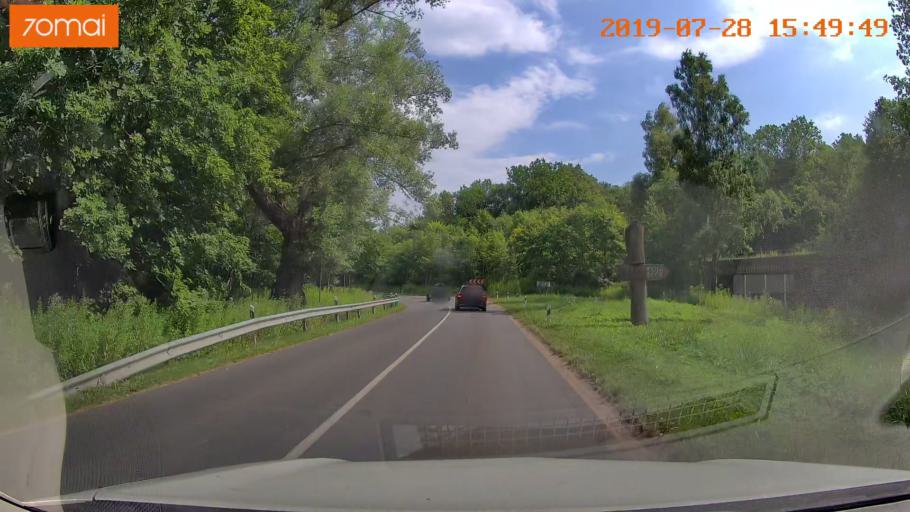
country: RU
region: Kaliningrad
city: Otradnoye
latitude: 54.9404
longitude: 20.0830
